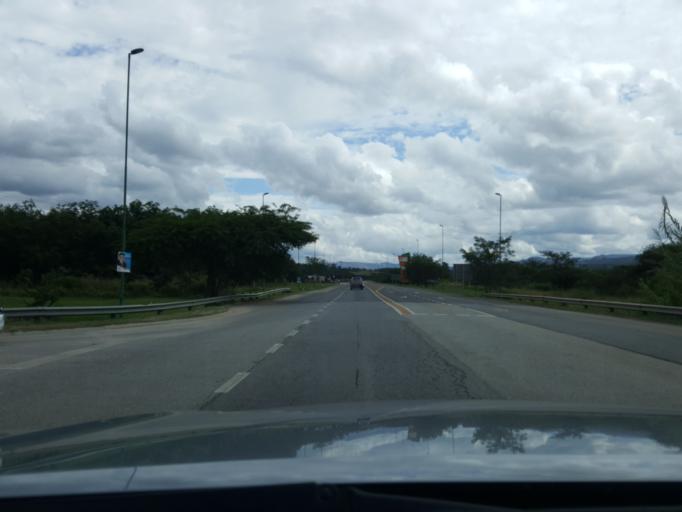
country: ZA
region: Mpumalanga
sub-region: Ehlanzeni District
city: Nelspruit
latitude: -25.4545
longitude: 30.9352
